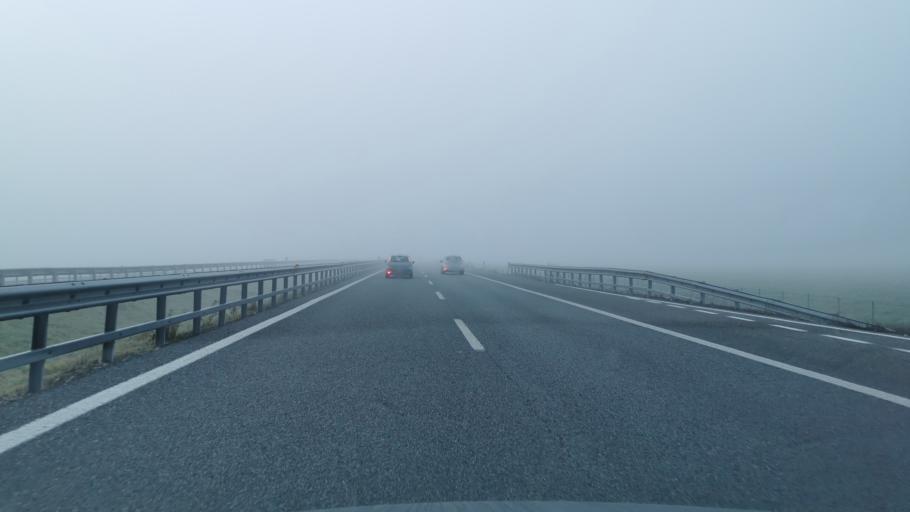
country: IT
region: Piedmont
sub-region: Provincia di Cuneo
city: Caramagna Piemonte
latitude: 44.7642
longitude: 7.7508
